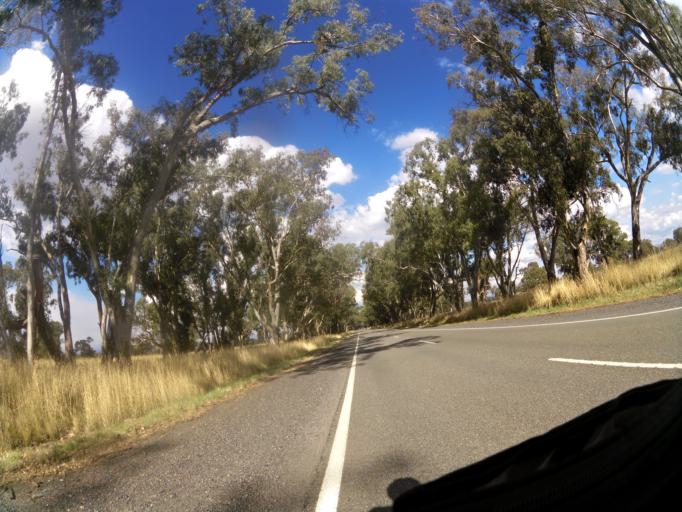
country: AU
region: Victoria
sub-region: Mansfield
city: Mansfield
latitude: -37.0015
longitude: 146.0729
